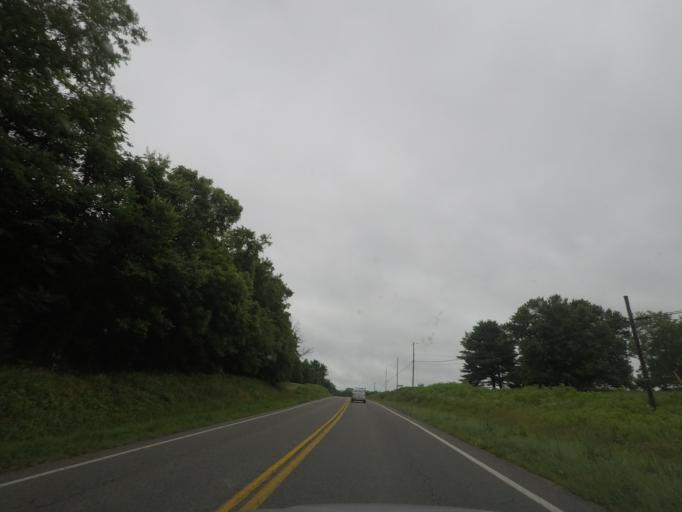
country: US
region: Virginia
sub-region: Fluvanna County
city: Palmyra
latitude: 37.8062
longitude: -78.2389
